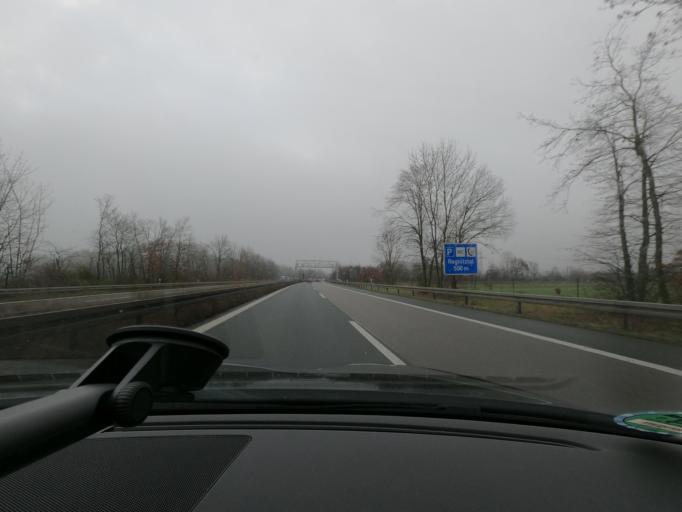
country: DE
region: Bavaria
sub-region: Upper Franconia
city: Eggolsheim
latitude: 49.7588
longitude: 11.0572
